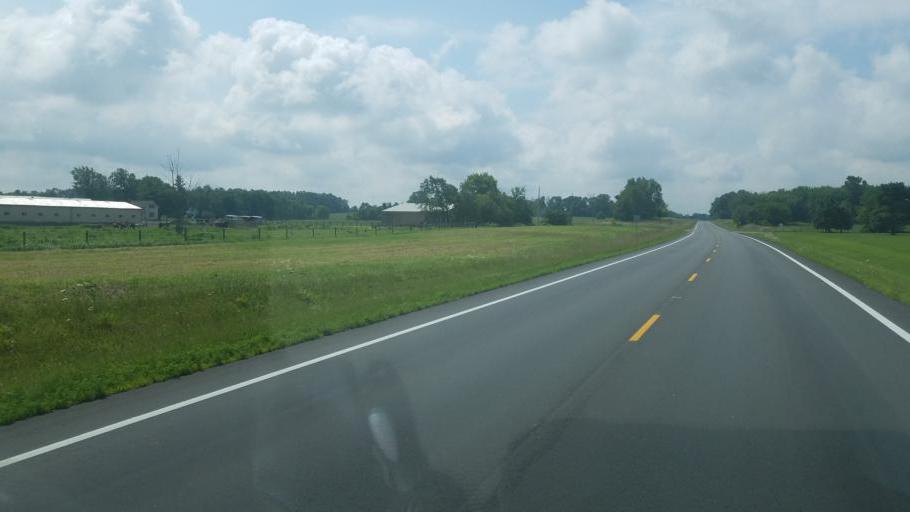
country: US
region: Ohio
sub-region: Fairfield County
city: Baltimore
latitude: 39.7996
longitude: -82.5735
